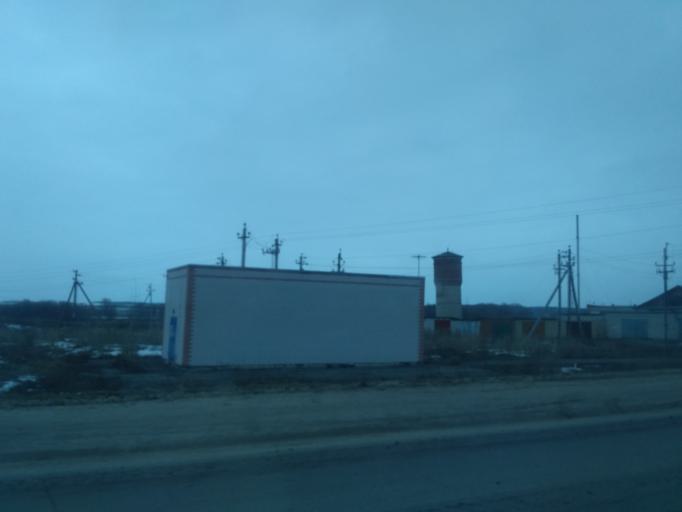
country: RU
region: Nizjnij Novgorod
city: Perevoz
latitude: 55.6025
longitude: 44.5582
